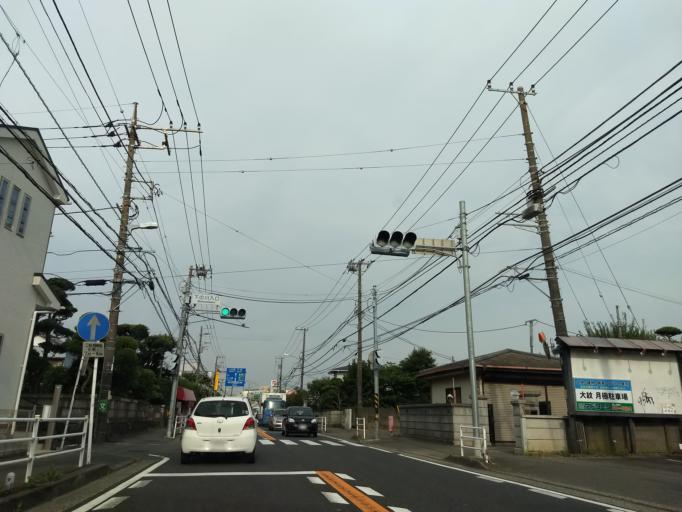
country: JP
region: Kanagawa
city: Chigasaki
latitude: 35.3331
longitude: 139.3806
